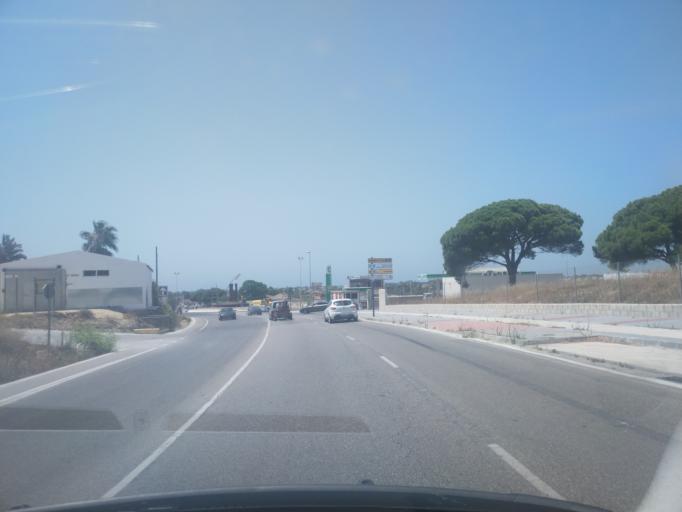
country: ES
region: Andalusia
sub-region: Provincia de Cadiz
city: Chiclana de la Frontera
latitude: 36.3939
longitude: -6.1454
